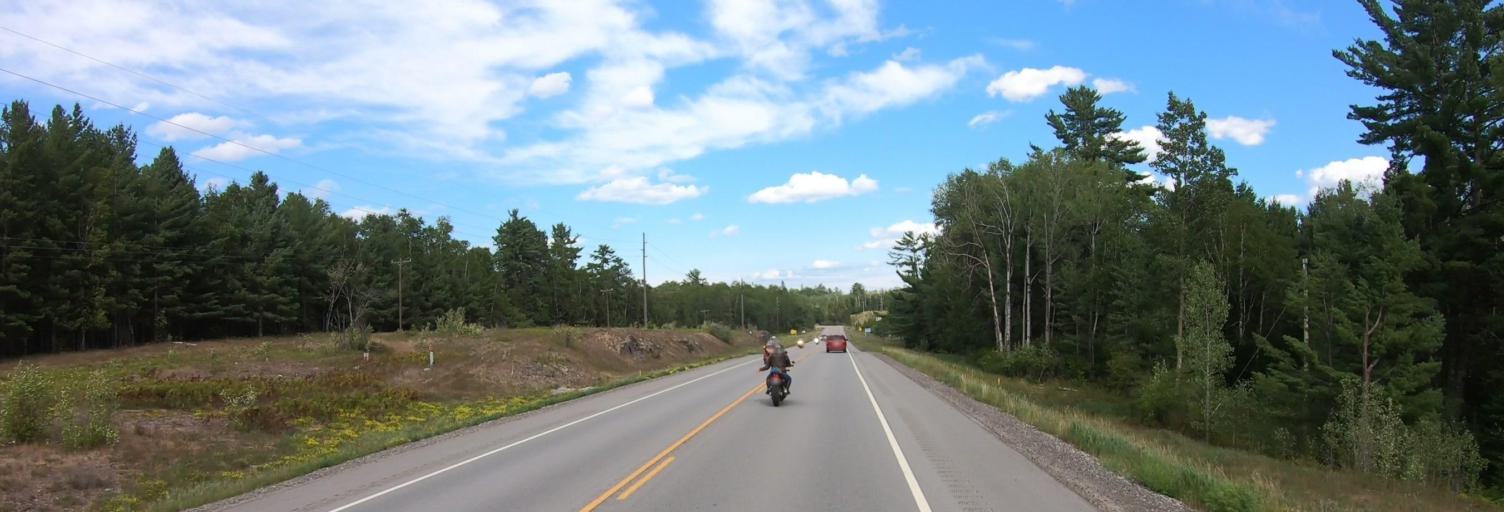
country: US
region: Minnesota
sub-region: Saint Louis County
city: Babbitt
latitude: 47.8537
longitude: -92.0556
